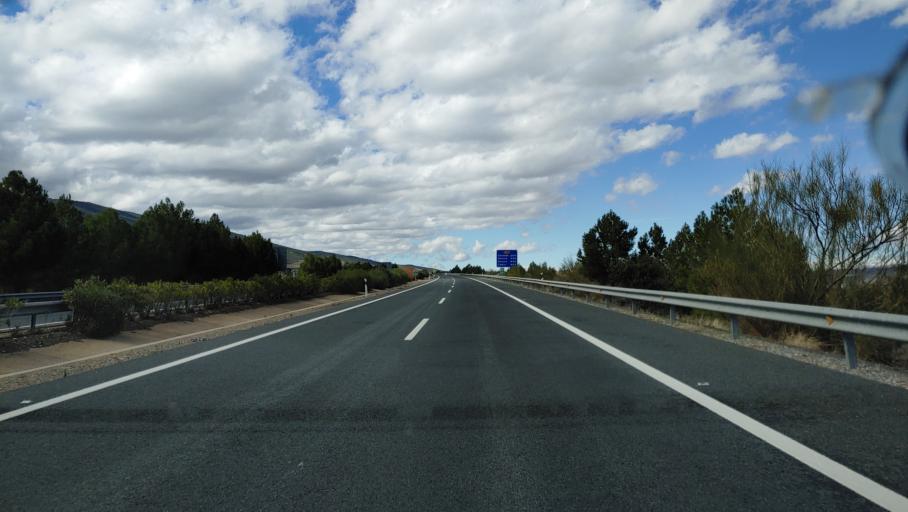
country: ES
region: Andalusia
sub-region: Provincia de Almeria
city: Abrucena
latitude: 37.1512
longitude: -2.8097
